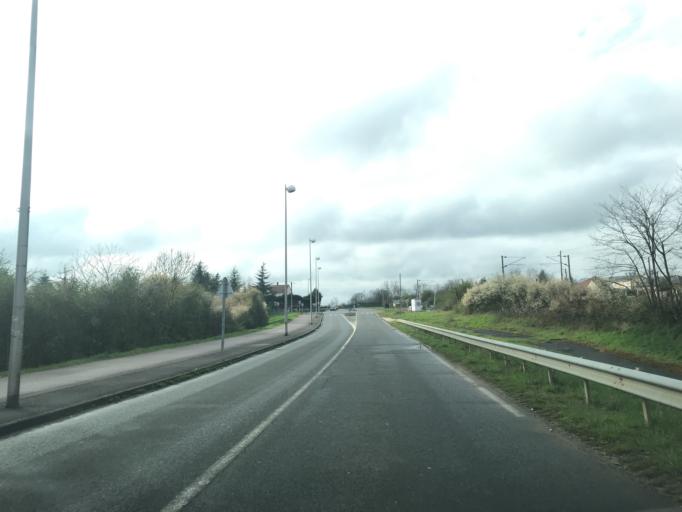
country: FR
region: Centre
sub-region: Departement du Loiret
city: Saint-Martin-sur-Ocre
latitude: 47.6853
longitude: 2.6558
